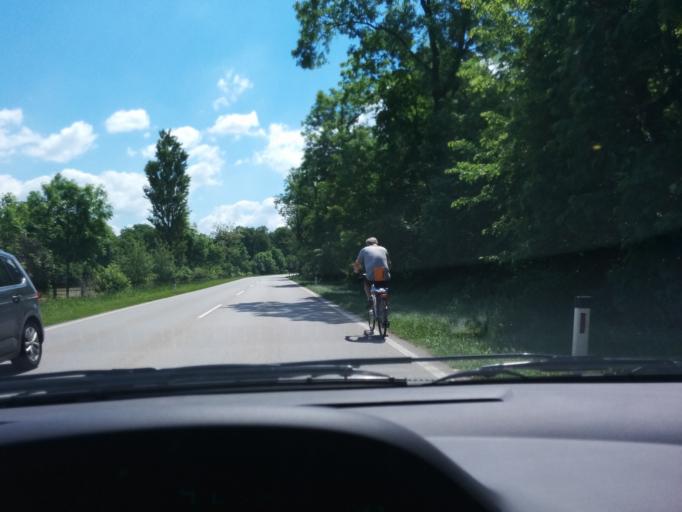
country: AT
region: Lower Austria
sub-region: Politischer Bezirk Baden
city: Ebreichsdorf
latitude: 47.9630
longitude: 16.3875
